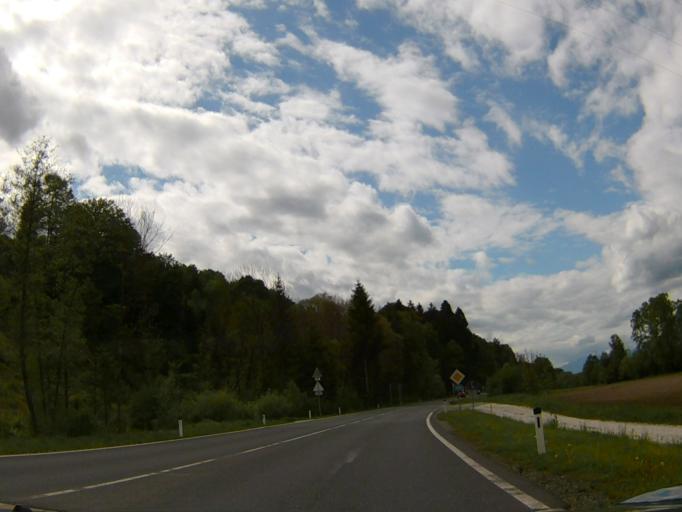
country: AT
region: Carinthia
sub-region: Villach Stadt
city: Villach
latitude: 46.6497
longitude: 13.7713
